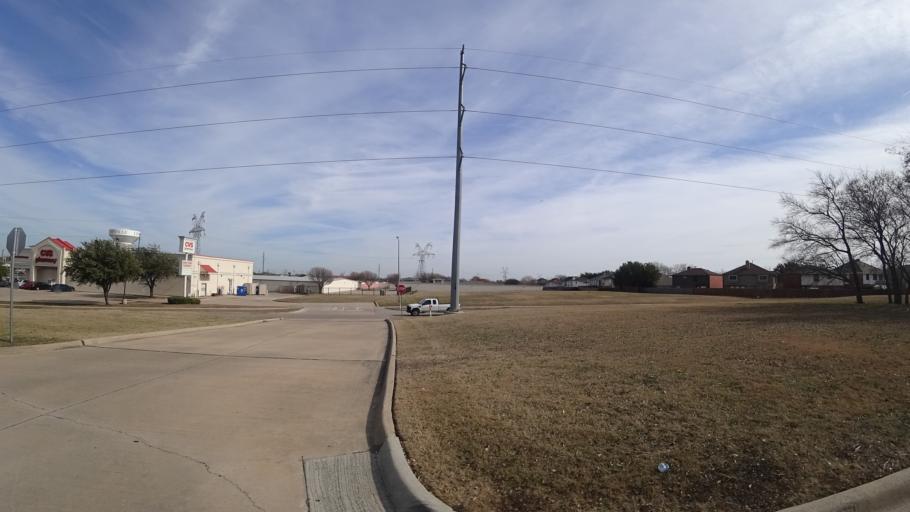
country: US
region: Texas
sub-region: Denton County
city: Highland Village
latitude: 33.0701
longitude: -97.0359
